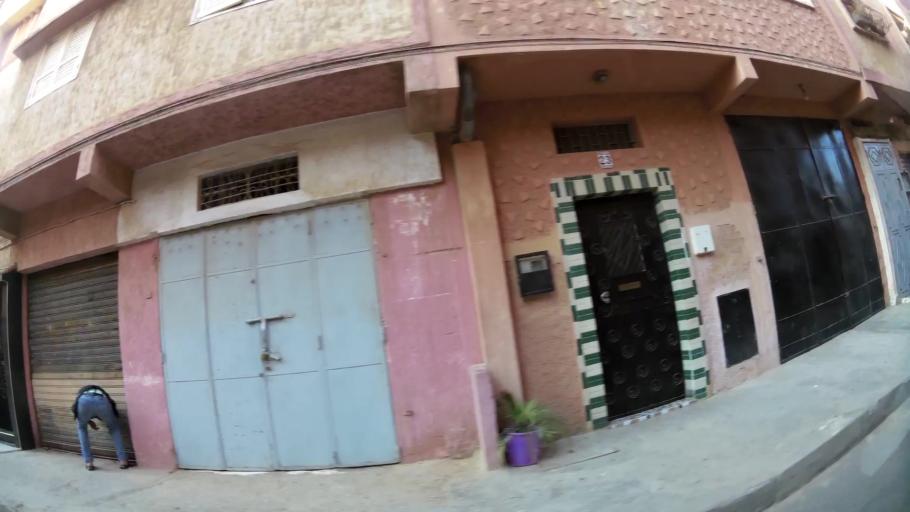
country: MA
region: Rabat-Sale-Zemmour-Zaer
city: Sale
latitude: 34.0543
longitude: -6.7895
